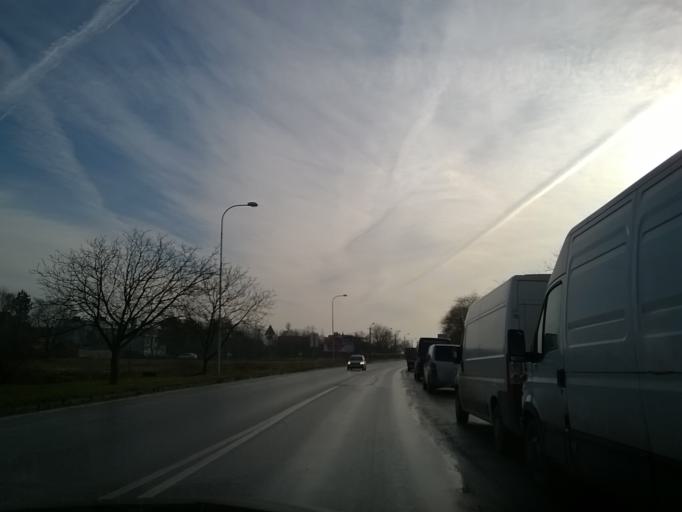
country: SK
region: Nitriansky
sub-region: Okres Nitra
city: Nitra
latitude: 48.2987
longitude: 18.0669
